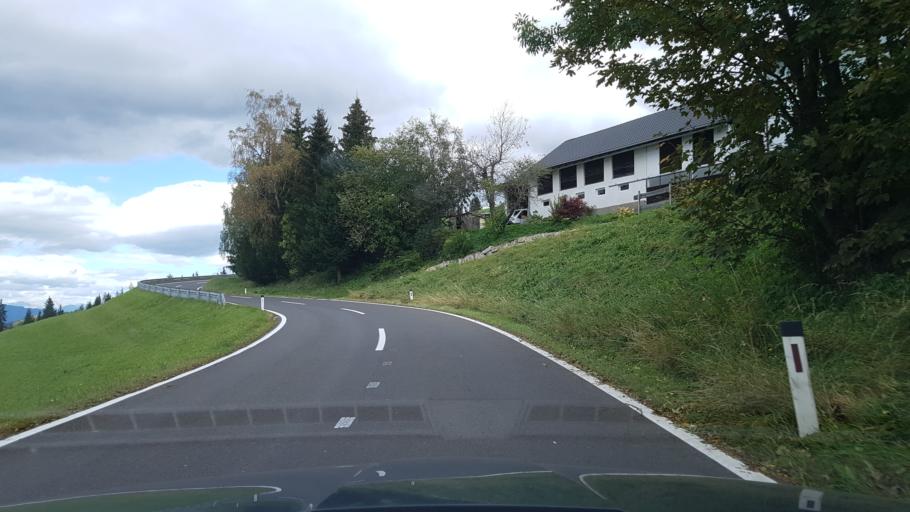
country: AT
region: Styria
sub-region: Politischer Bezirk Murtal
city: Kleinlobming
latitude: 47.1418
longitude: 14.8130
